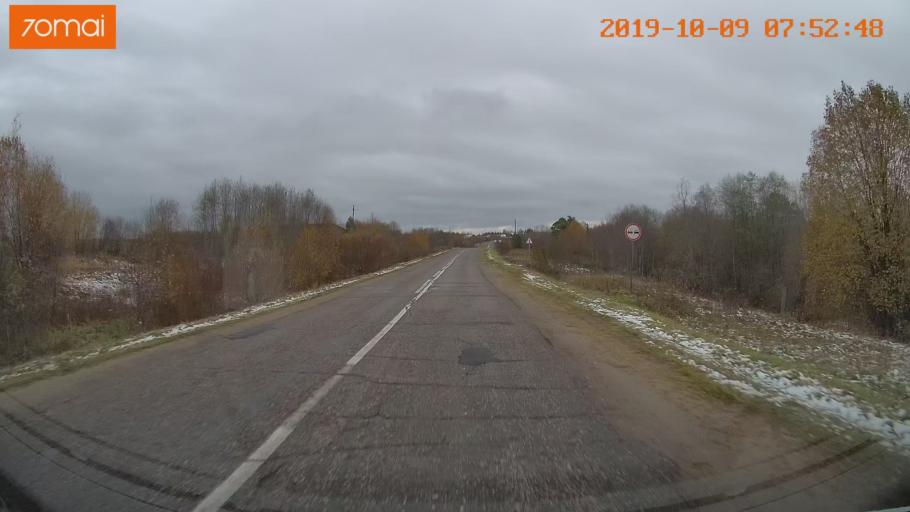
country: RU
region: Jaroslavl
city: Kukoboy
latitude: 58.6941
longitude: 39.8900
